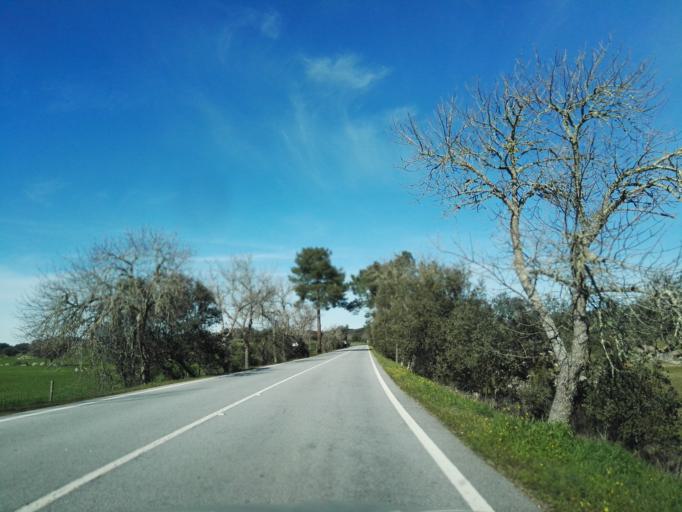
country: PT
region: Portalegre
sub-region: Arronches
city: Arronches
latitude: 39.0658
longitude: -7.2760
